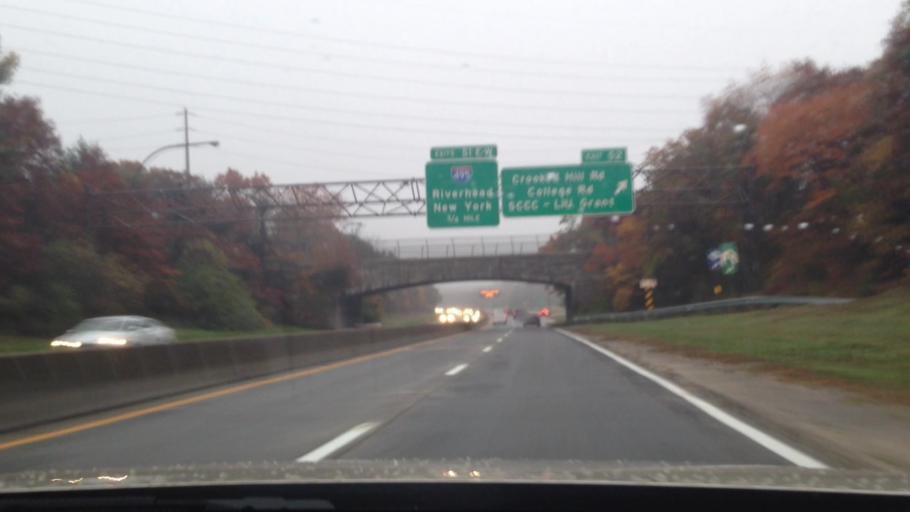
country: US
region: New York
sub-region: Suffolk County
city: Brentwood
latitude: 40.7916
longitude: -73.2786
